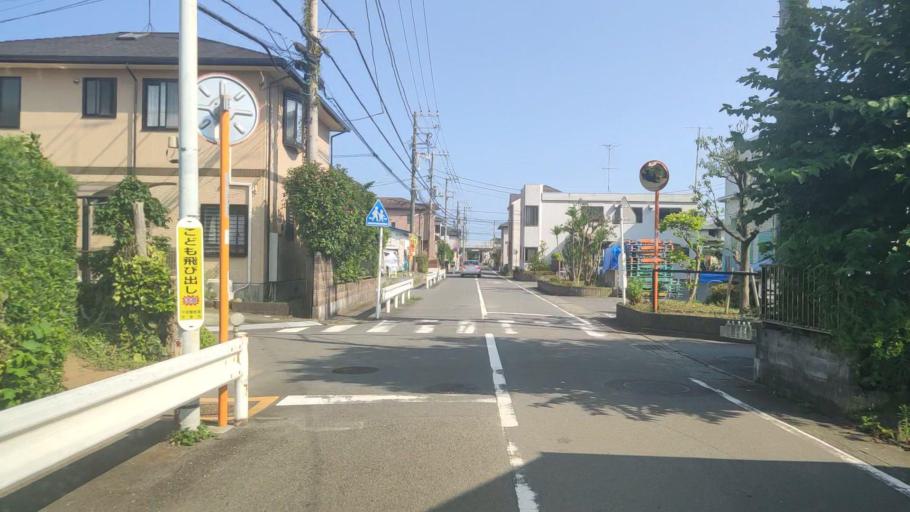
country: JP
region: Kanagawa
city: Hiratsuka
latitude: 35.3290
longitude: 139.3257
